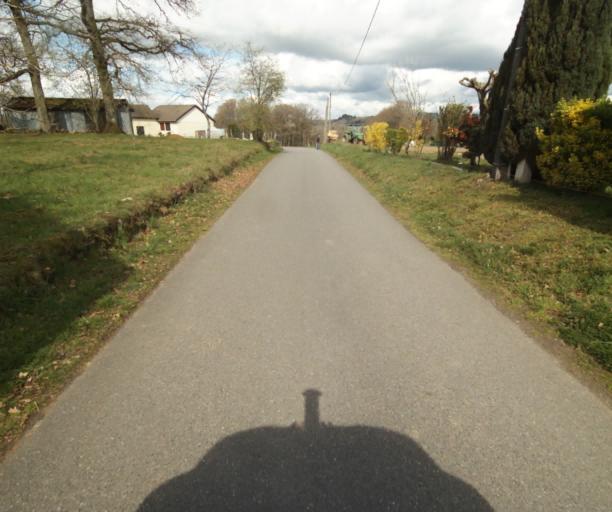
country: FR
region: Limousin
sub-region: Departement de la Correze
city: Correze
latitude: 45.3678
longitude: 1.8926
